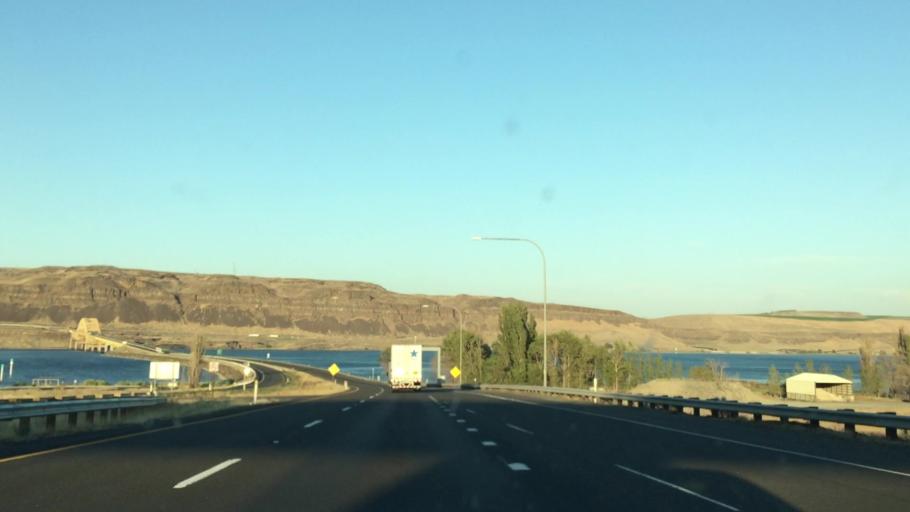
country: US
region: Washington
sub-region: Grant County
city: Mattawa
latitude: 46.9404
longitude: -119.9876
